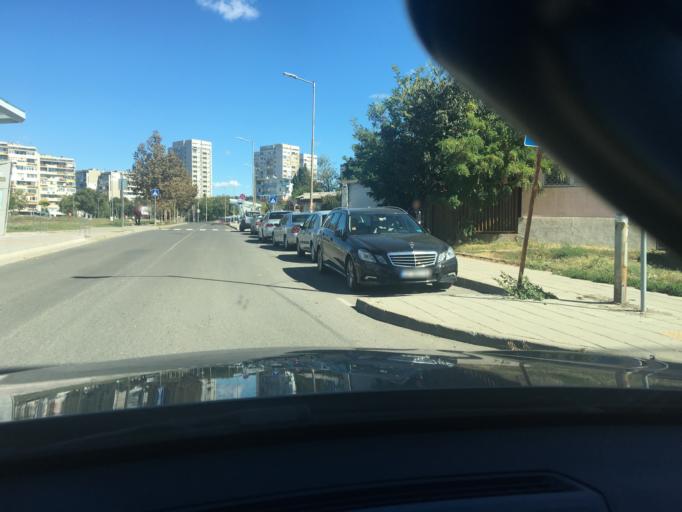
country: BG
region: Burgas
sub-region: Obshtina Burgas
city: Burgas
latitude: 42.5243
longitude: 27.4635
